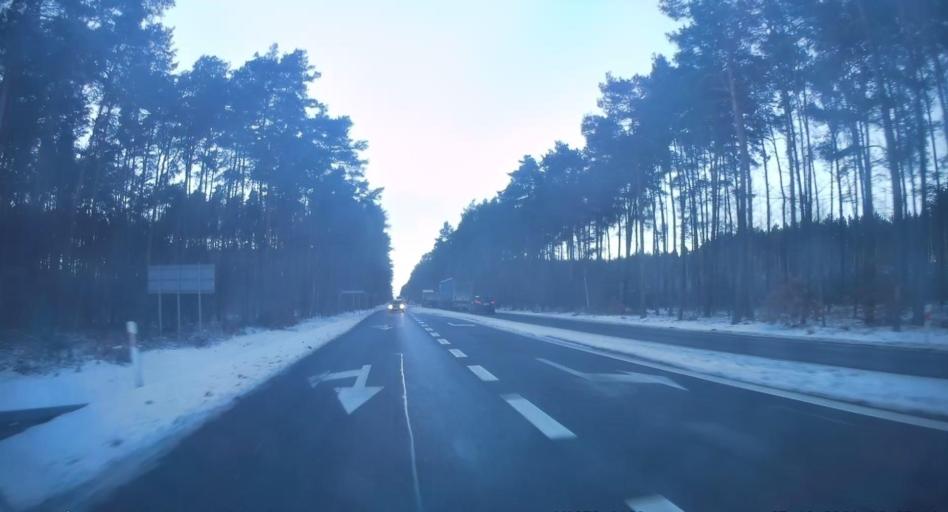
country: PL
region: Swietokrzyskie
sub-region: Powiat konecki
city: Ruda Maleniecka
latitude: 51.1451
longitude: 20.2438
